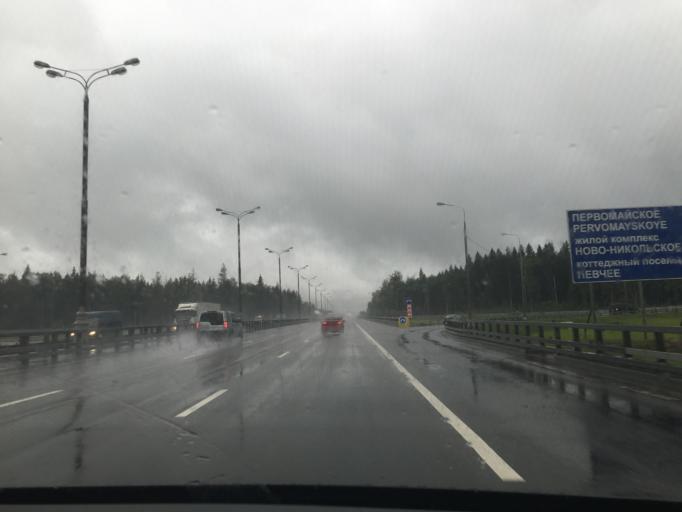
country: RU
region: Moskovskaya
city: Kokoshkino
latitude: 55.5570
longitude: 37.1507
